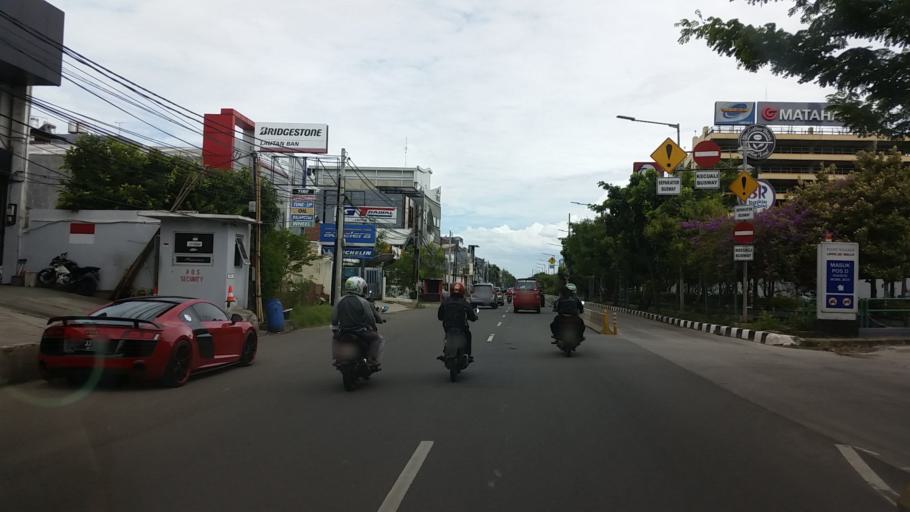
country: ID
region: Jakarta Raya
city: Jakarta
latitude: -6.1158
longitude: 106.7866
